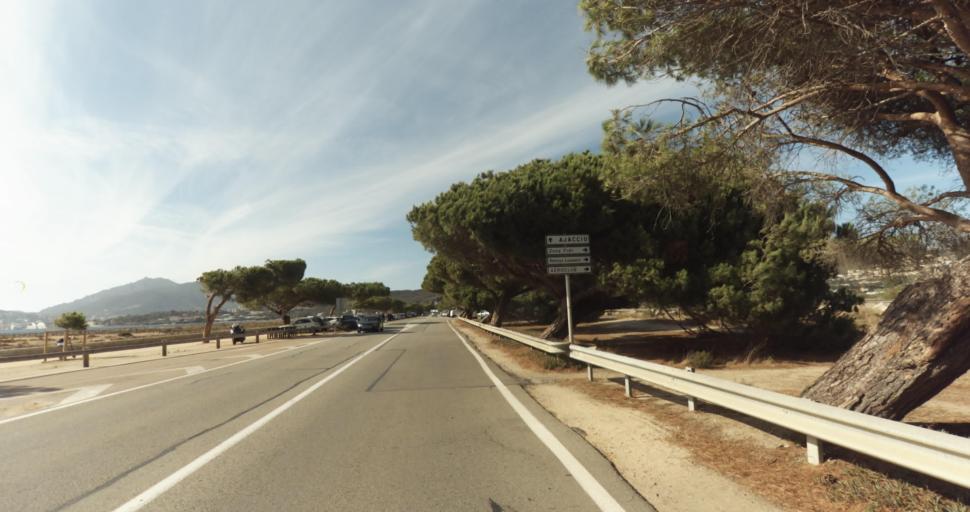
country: FR
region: Corsica
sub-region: Departement de la Corse-du-Sud
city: Ajaccio
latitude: 41.9204
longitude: 8.7882
